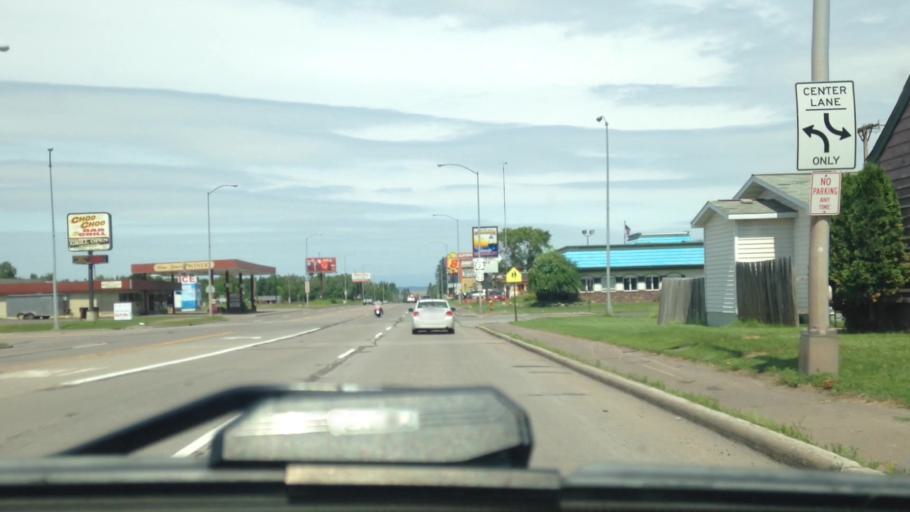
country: US
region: Wisconsin
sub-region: Douglas County
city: Superior
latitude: 46.6776
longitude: -92.0102
